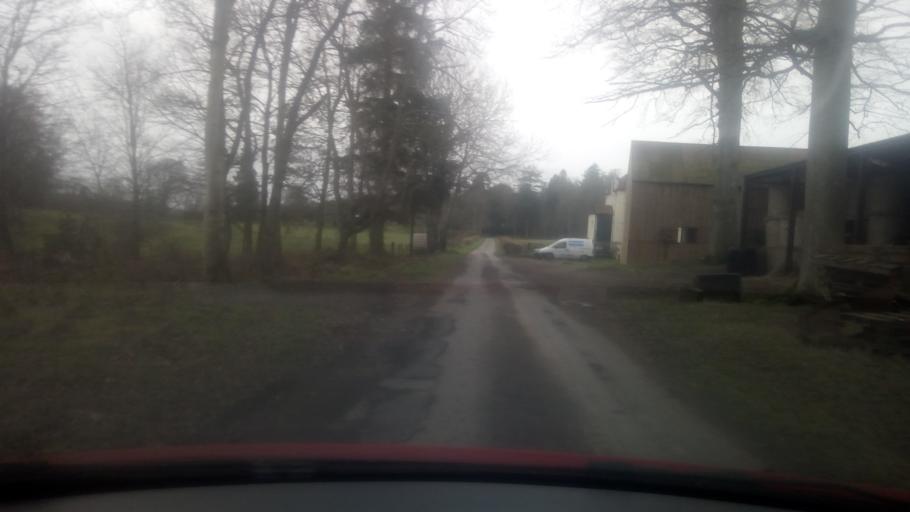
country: GB
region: Scotland
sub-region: The Scottish Borders
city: Jedburgh
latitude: 55.4489
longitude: -2.6399
